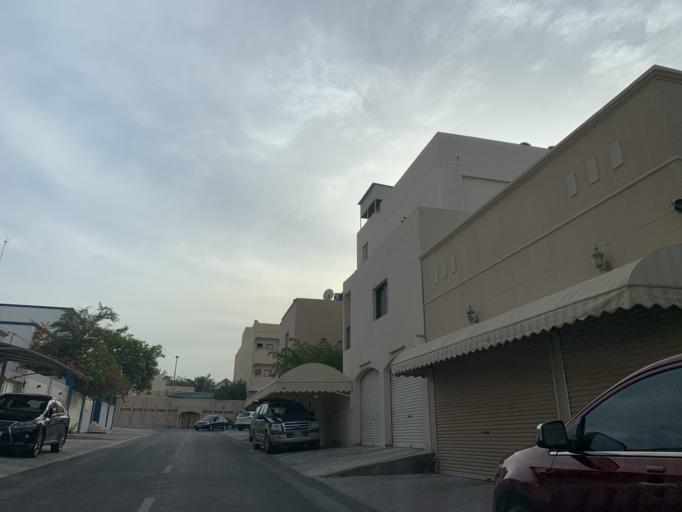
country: BH
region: Northern
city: Ar Rifa'
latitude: 26.1227
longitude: 50.5843
